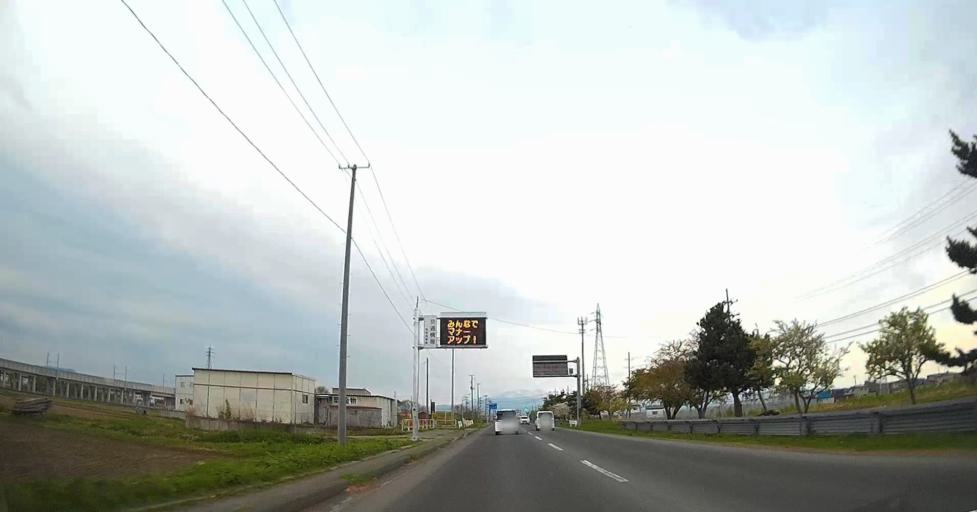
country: JP
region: Aomori
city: Aomori Shi
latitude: 40.8449
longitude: 140.6858
